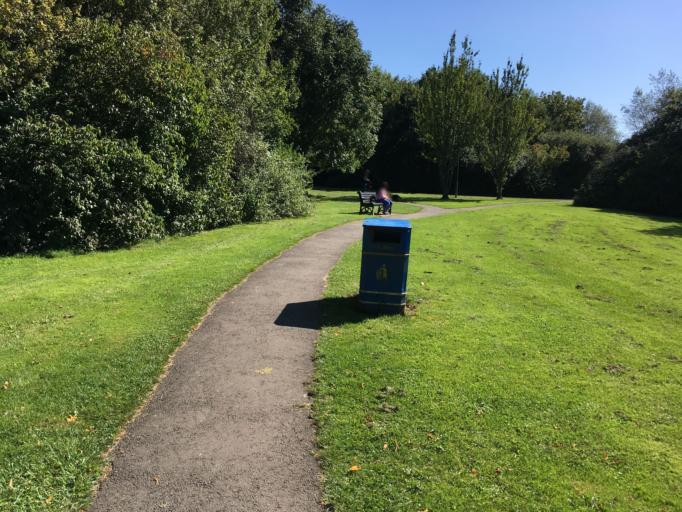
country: GB
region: England
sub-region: South Gloucestershire
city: Yate
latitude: 51.5566
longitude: -2.4119
